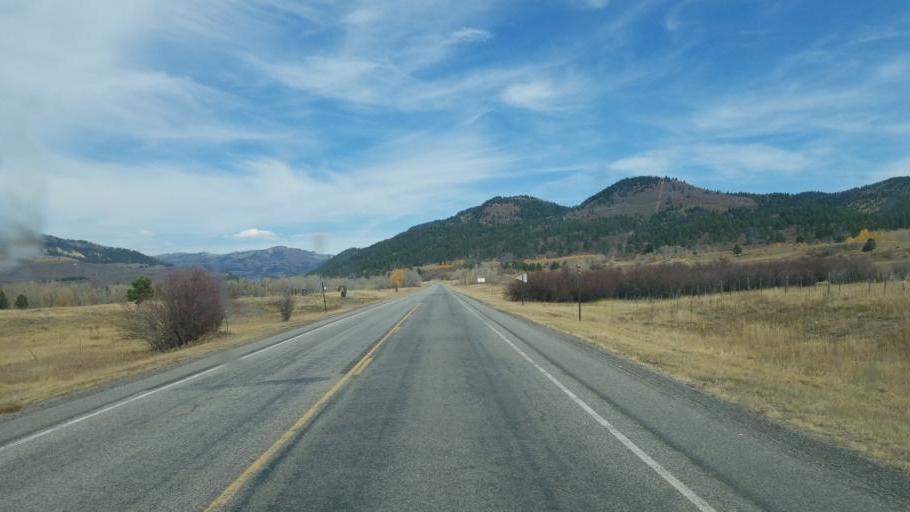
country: US
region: New Mexico
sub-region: Rio Arriba County
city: Chama
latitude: 36.9136
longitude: -106.5678
